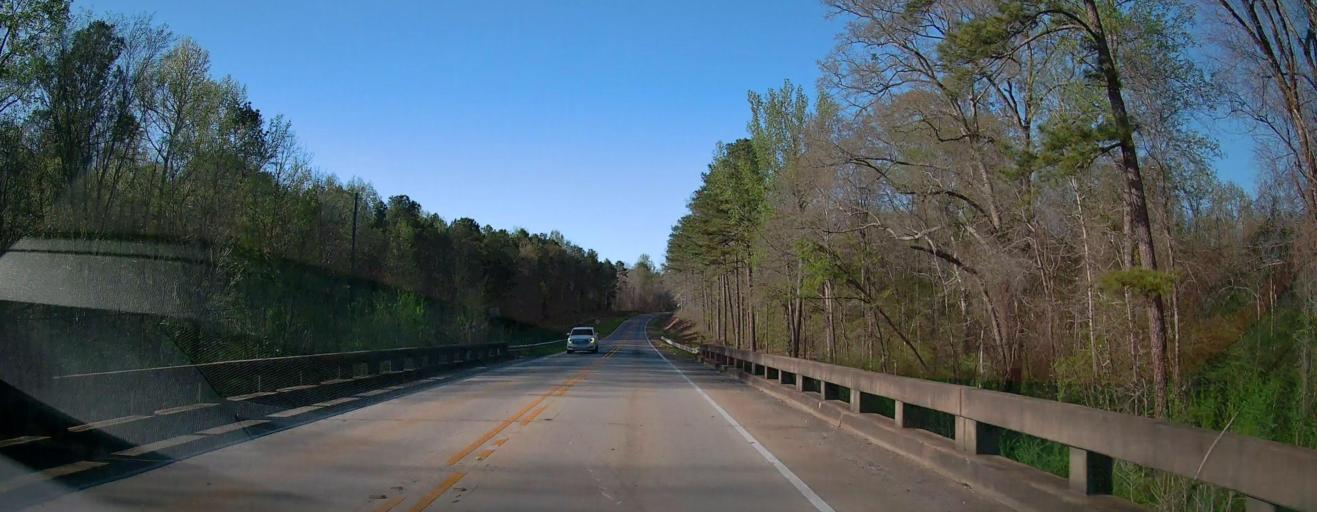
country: US
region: Georgia
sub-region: Monroe County
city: Forsyth
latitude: 33.1218
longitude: -83.9434
